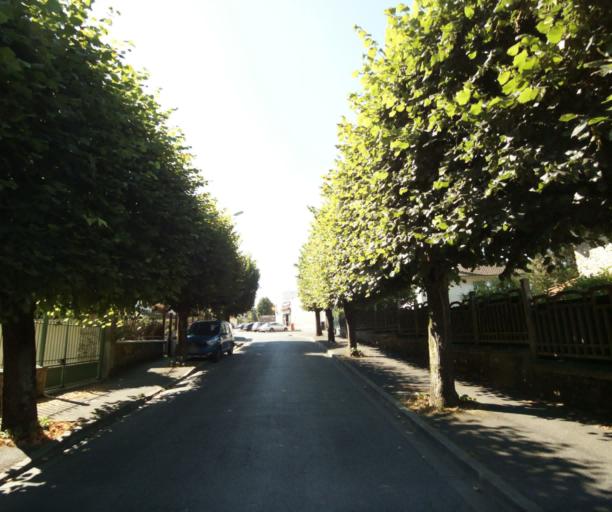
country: FR
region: Ile-de-France
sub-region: Departement de Seine-et-Marne
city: Lagny-sur-Marne
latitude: 48.8715
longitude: 2.7043
